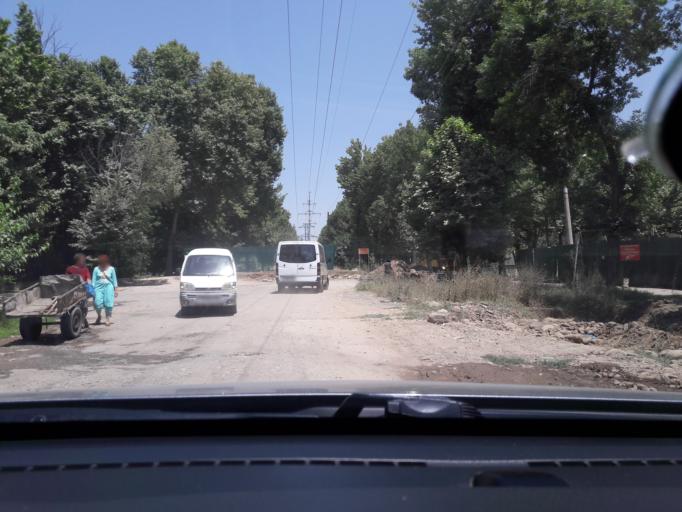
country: TJ
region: Dushanbe
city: Dushanbe
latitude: 38.5874
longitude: 68.7549
